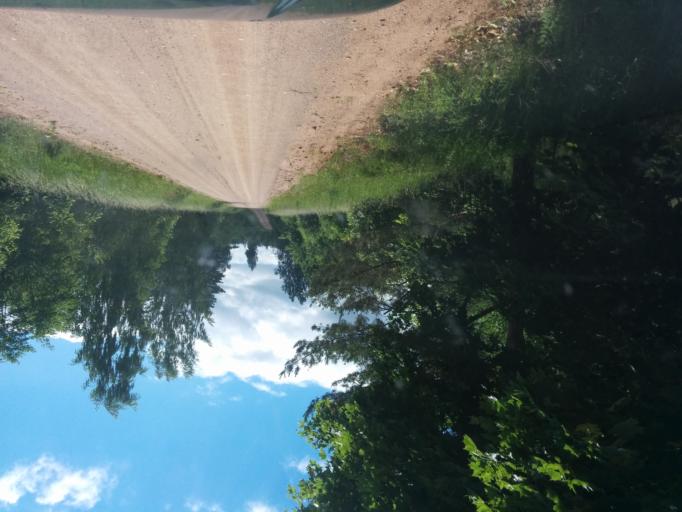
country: LV
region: Vilaka
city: Vilaka
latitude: 57.3347
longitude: 27.7347
